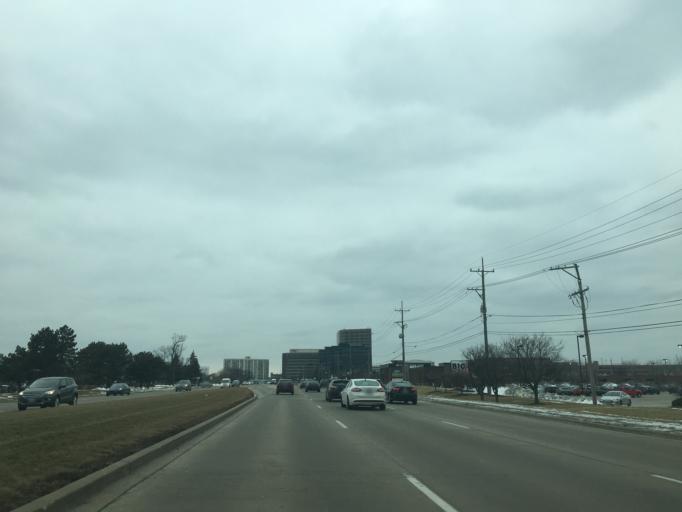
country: US
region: Illinois
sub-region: DuPage County
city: Oakbrook Terrace
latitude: 41.8463
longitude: -87.9751
